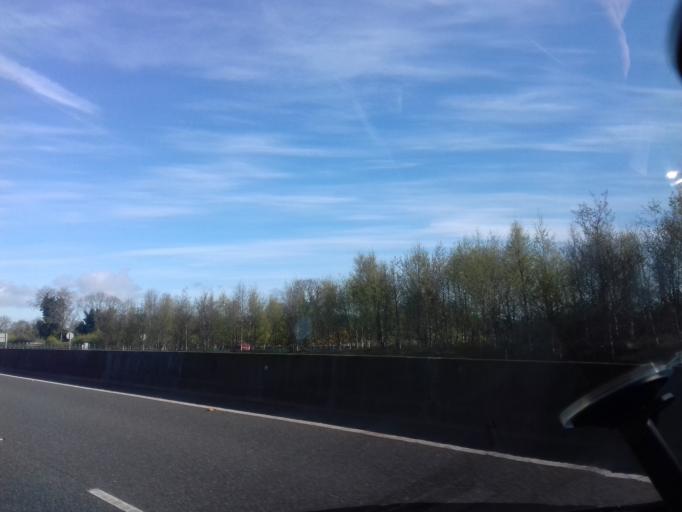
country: IE
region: Leinster
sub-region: An Mhi
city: Navan
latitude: 53.6408
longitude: -6.7424
